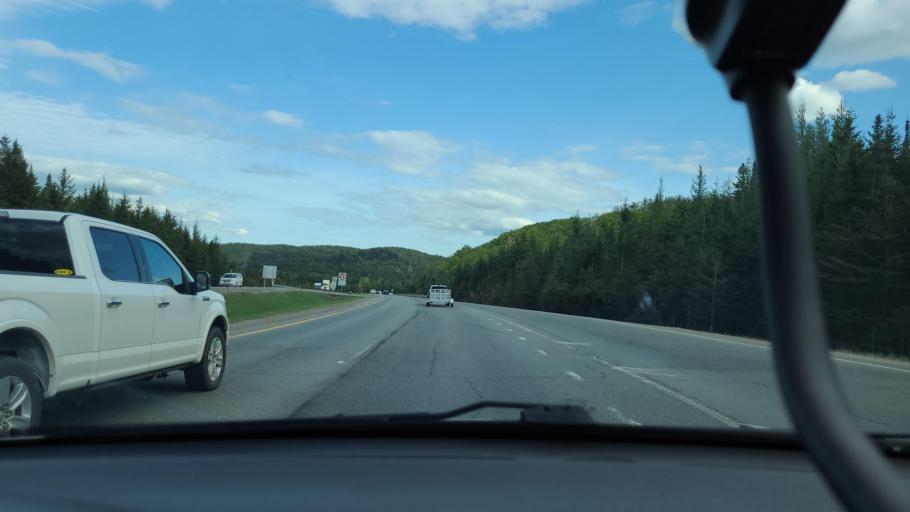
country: CA
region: Quebec
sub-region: Laurentides
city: Sainte-Agathe-des-Monts
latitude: 46.0346
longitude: -74.2687
